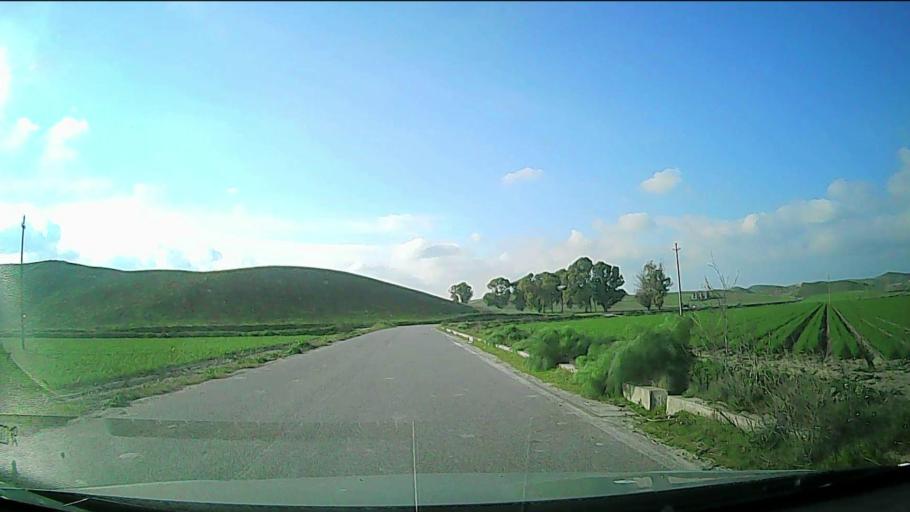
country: IT
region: Calabria
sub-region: Provincia di Crotone
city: Rocca di Neto
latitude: 39.1975
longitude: 17.0650
